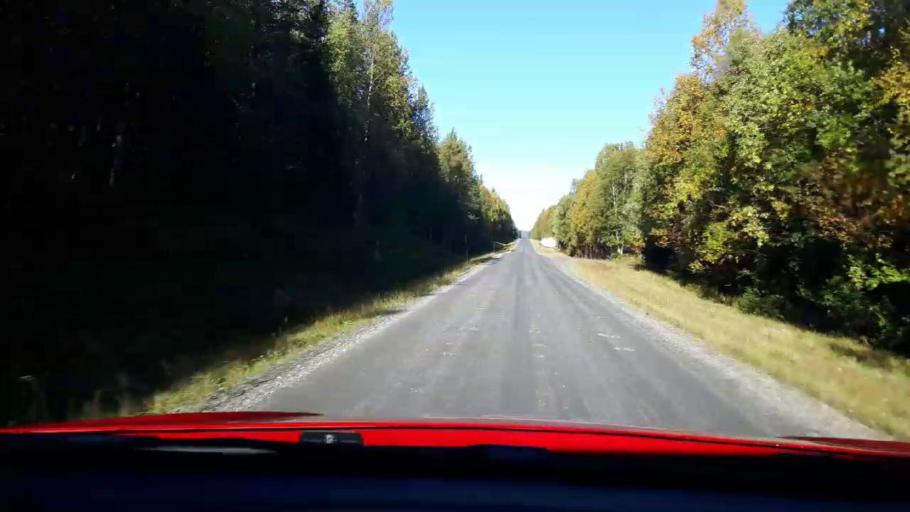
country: NO
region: Nord-Trondelag
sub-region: Lierne
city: Sandvika
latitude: 64.5402
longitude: 14.0024
